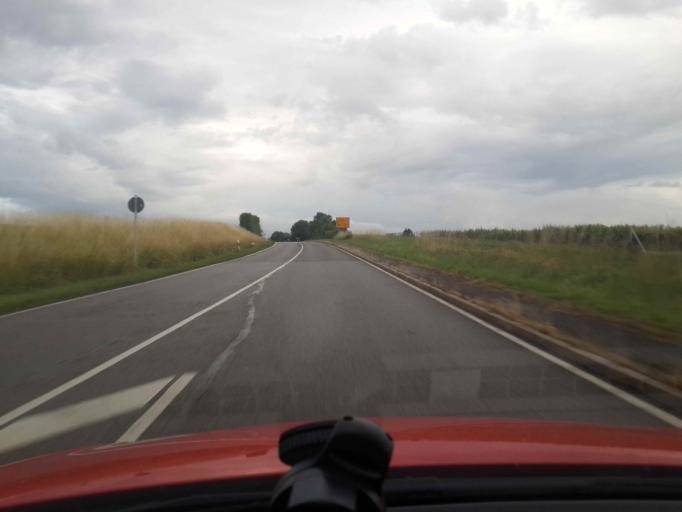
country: DE
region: Baden-Wuerttemberg
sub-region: Regierungsbezirk Stuttgart
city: Oedheim
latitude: 49.2494
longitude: 9.2153
